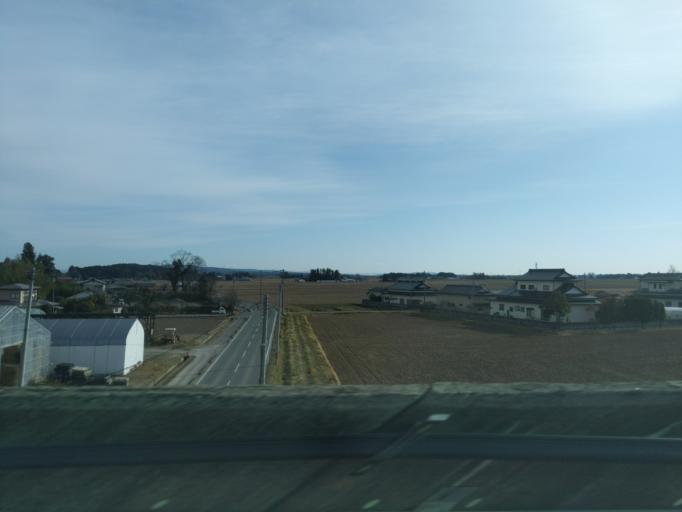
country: JP
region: Miyagi
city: Furukawa
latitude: 38.6132
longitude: 140.9918
